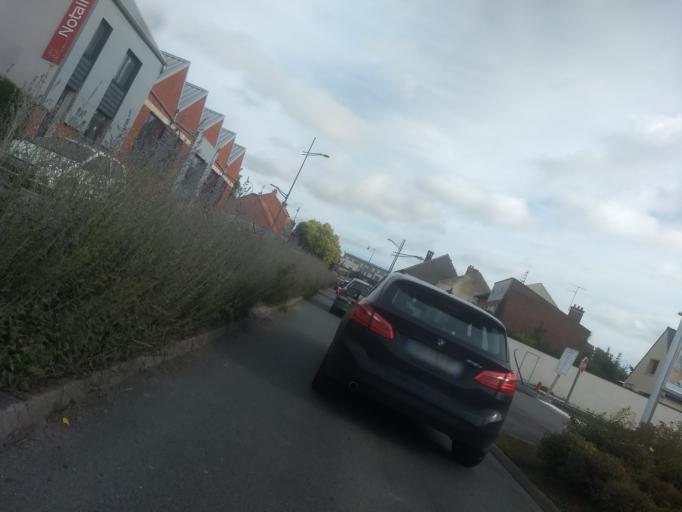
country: FR
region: Nord-Pas-de-Calais
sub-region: Departement du Pas-de-Calais
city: Dainville
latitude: 50.2864
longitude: 2.7436
